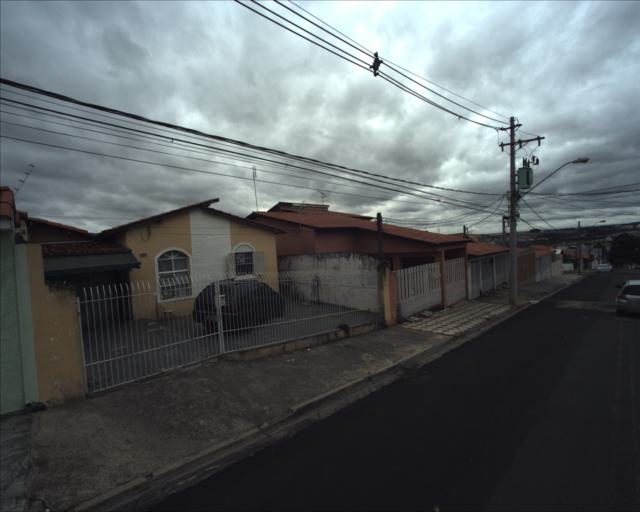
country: BR
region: Sao Paulo
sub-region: Sorocaba
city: Sorocaba
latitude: -23.4795
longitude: -47.4645
